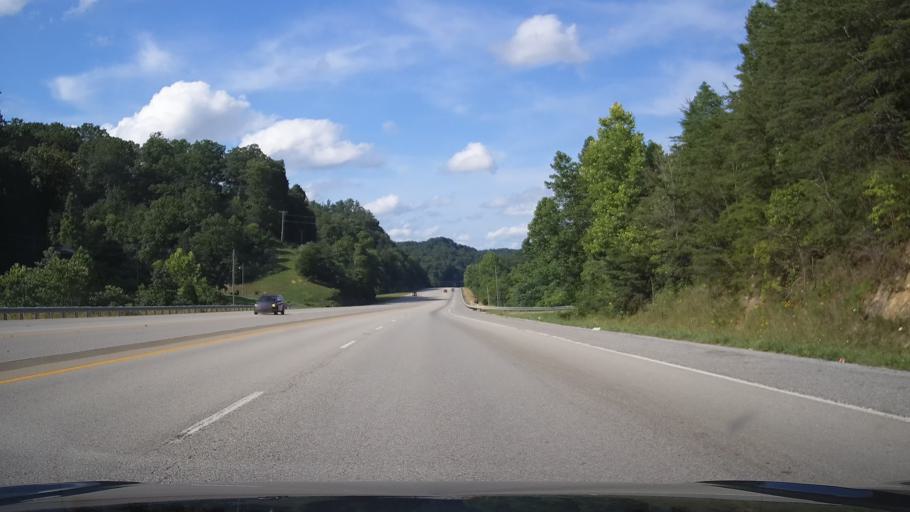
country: US
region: Kentucky
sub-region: Lawrence County
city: Louisa
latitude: 38.0395
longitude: -82.6490
